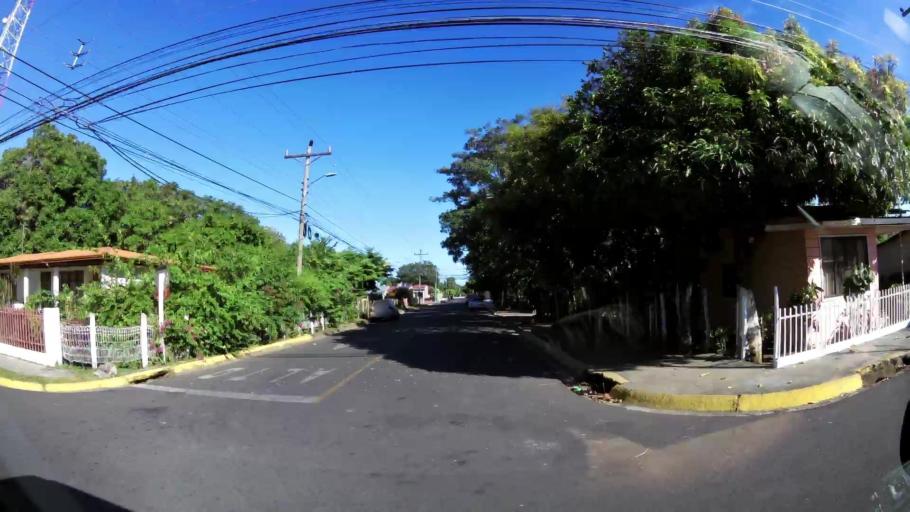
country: CR
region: Guanacaste
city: Belen
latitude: 10.4451
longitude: -85.5528
